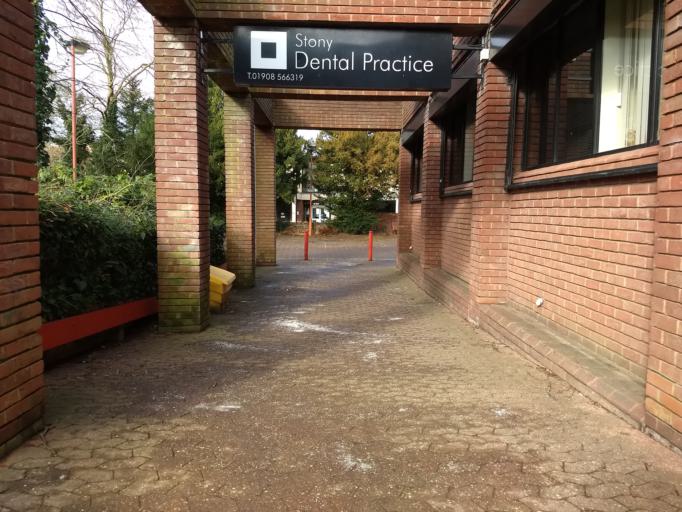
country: GB
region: England
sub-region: Milton Keynes
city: Stony Stratford
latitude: 52.0558
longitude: -0.8527
